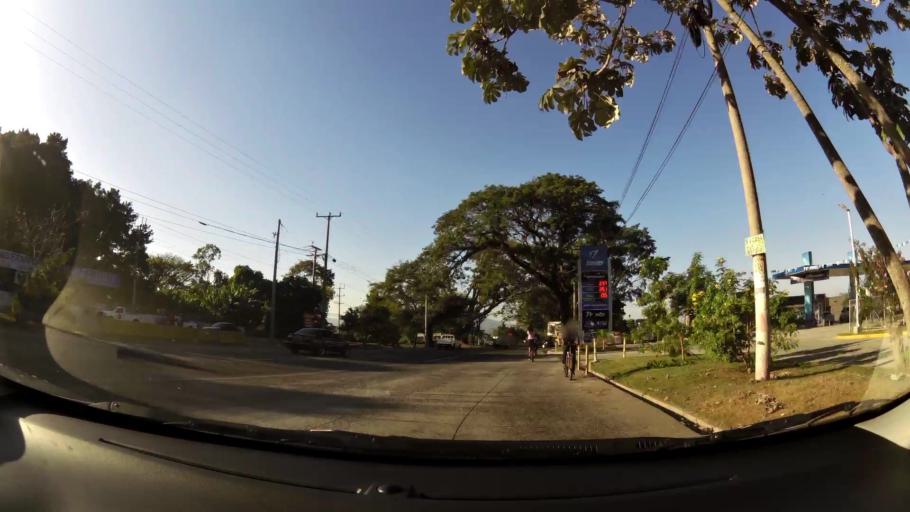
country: SV
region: La Libertad
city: Santa Tecla
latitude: 13.7377
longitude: -89.3614
